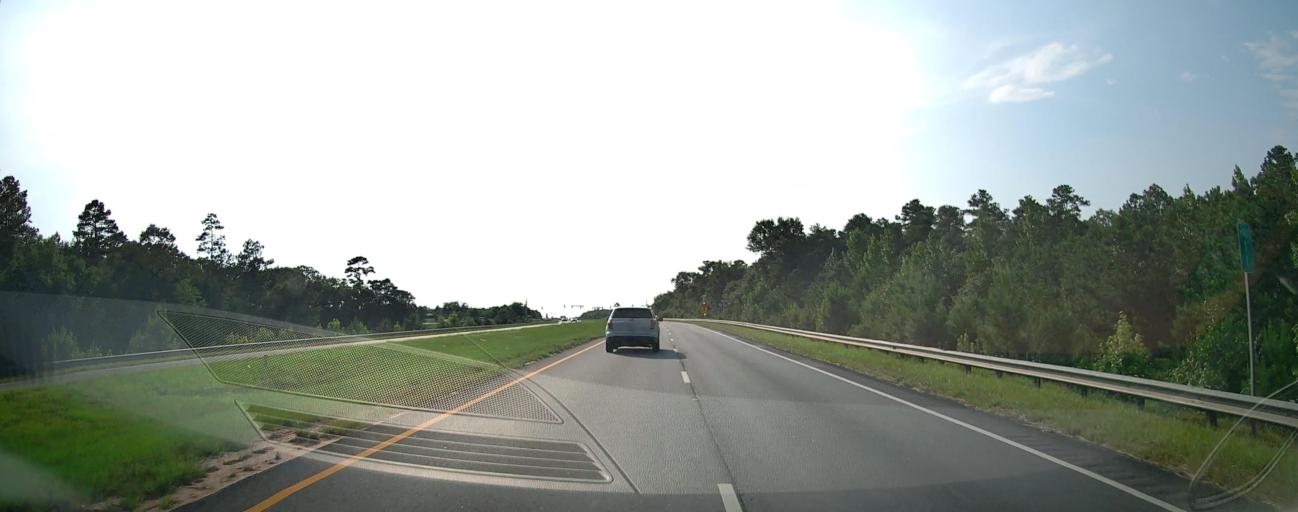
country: US
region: Georgia
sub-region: Taylor County
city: Butler
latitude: 32.5431
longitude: -84.2386
